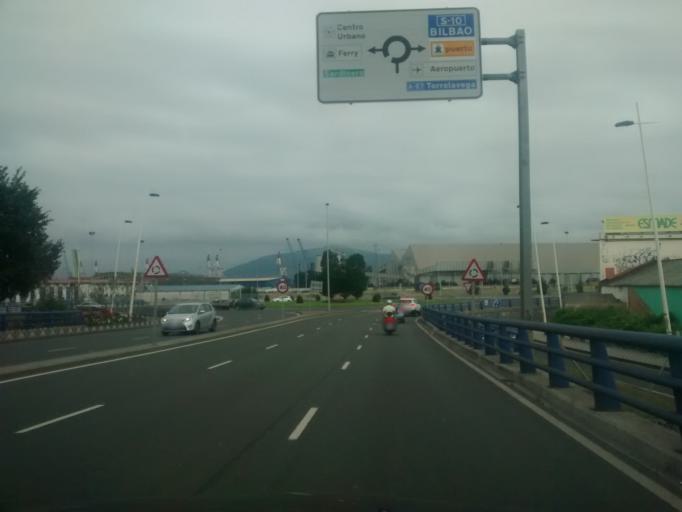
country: ES
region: Cantabria
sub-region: Provincia de Cantabria
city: Santander
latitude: 43.4526
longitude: -3.8279
